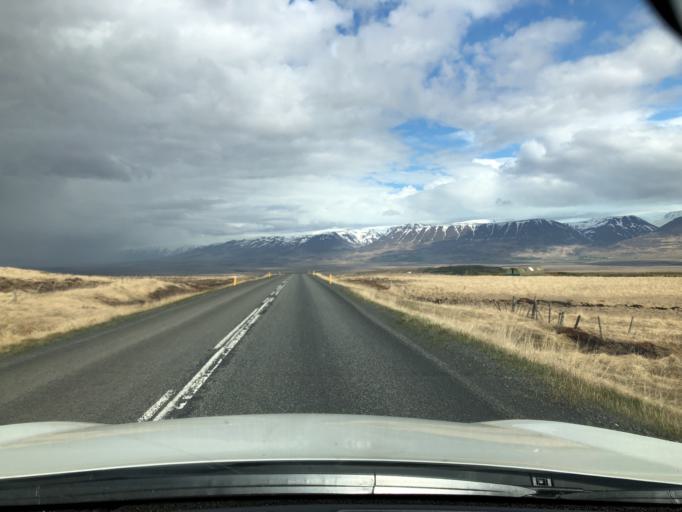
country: IS
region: Northwest
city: Saudarkrokur
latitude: 65.5390
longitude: -19.5051
